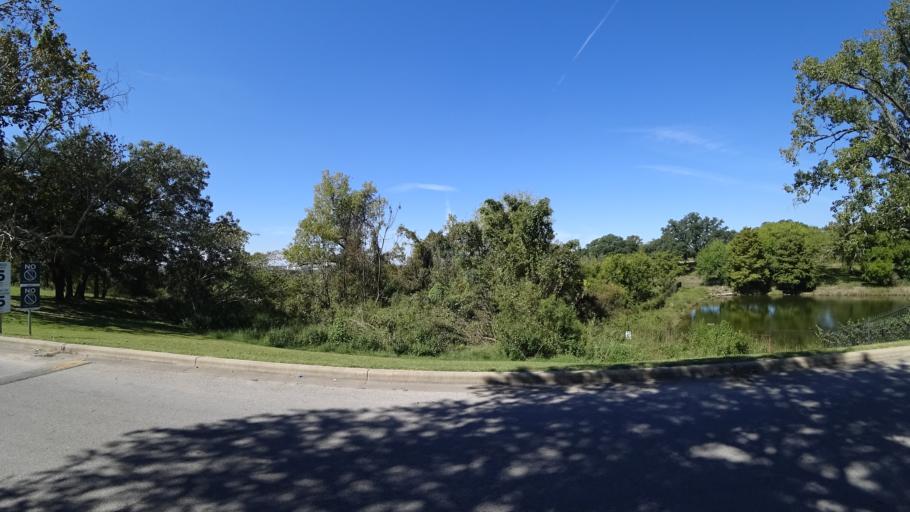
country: US
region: Texas
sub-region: Travis County
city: Hornsby Bend
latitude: 30.2749
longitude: -97.6386
